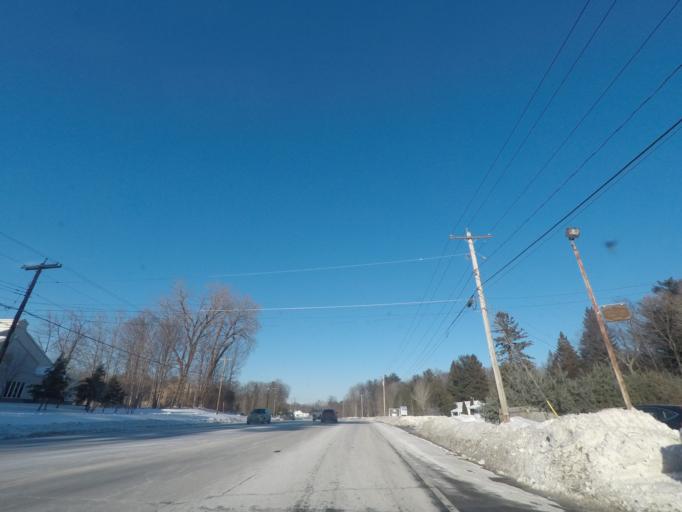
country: US
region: New York
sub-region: Saratoga County
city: Ballston Spa
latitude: 42.9786
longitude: -73.7882
